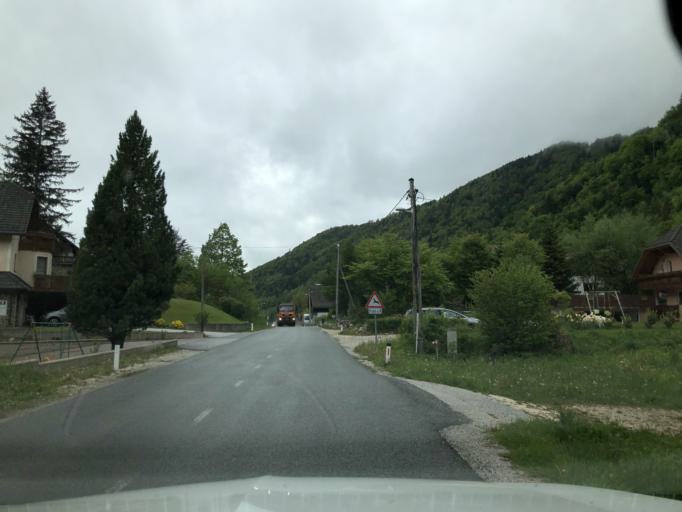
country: SI
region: Jesenice
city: Slovenski Javornik
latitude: 46.4173
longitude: 14.0824
